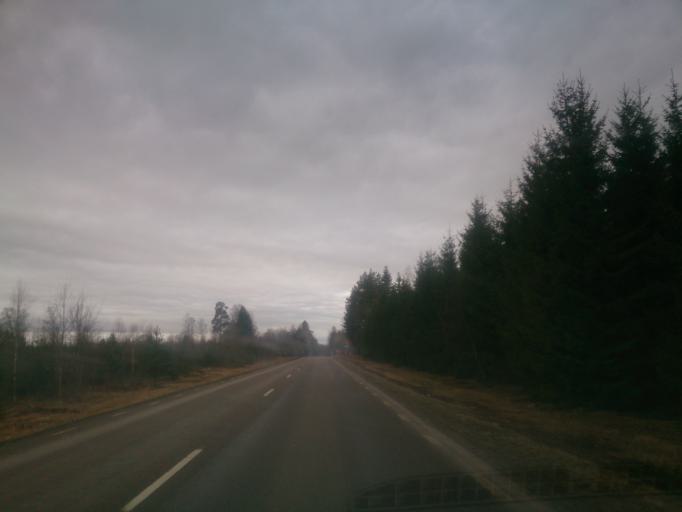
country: SE
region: OEstergoetland
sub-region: Motala Kommun
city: Borensberg
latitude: 58.4854
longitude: 15.2811
